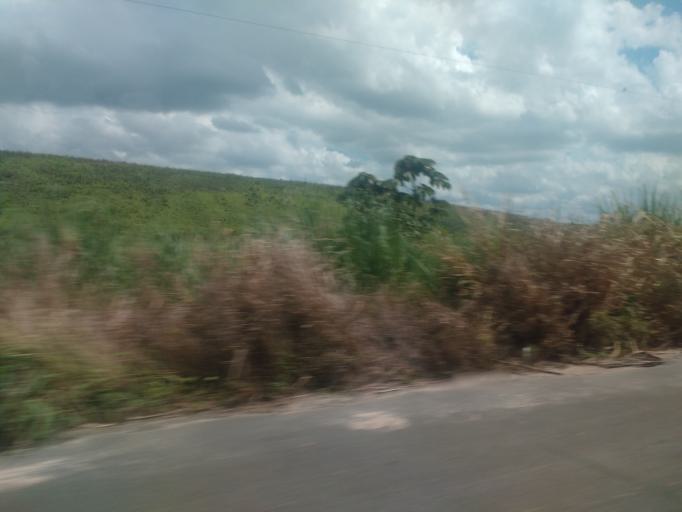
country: BR
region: Alagoas
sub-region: Messias
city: Messias
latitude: -9.3690
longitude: -35.8419
